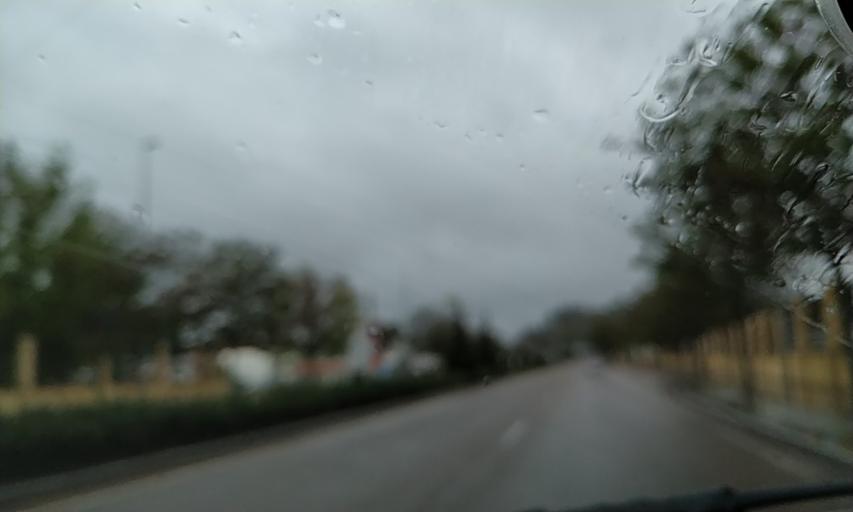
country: ES
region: Extremadura
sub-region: Provincia de Badajoz
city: Badajoz
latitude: 38.8941
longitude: -6.9705
